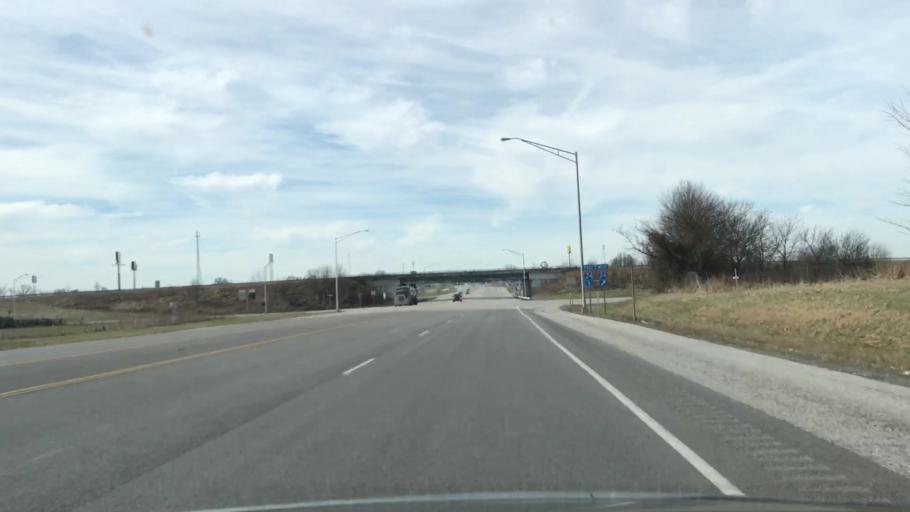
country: US
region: Kentucky
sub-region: Trigg County
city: Cadiz
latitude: 36.8840
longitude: -87.7338
